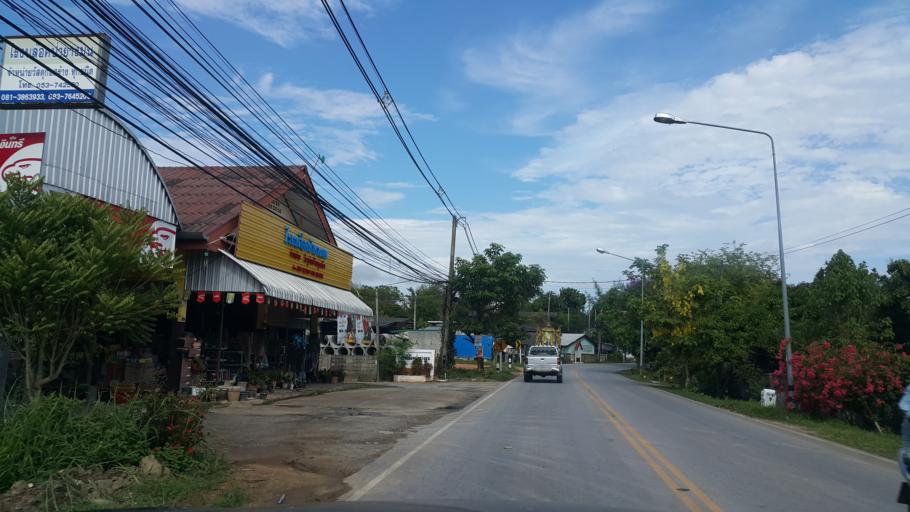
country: TH
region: Chiang Rai
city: Chiang Rai
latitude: 19.9119
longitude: 99.8761
